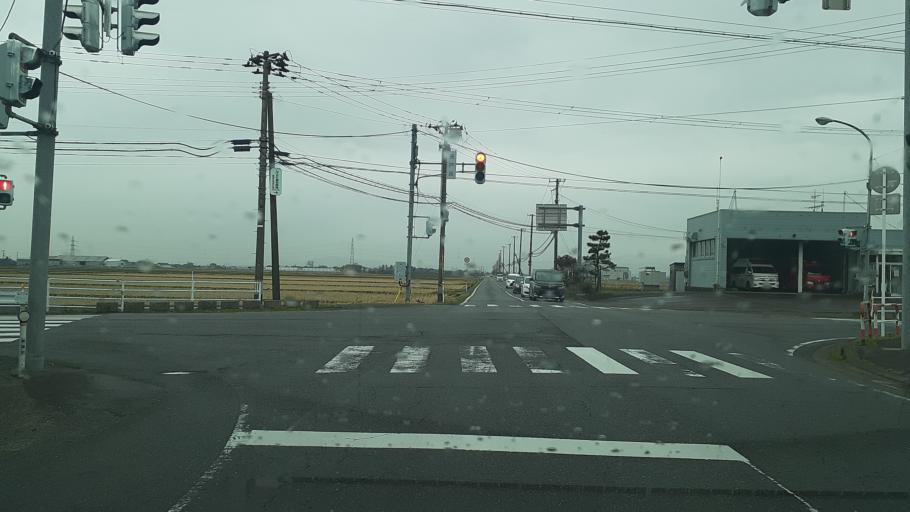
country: JP
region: Niigata
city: Suibara
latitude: 37.8847
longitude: 139.1772
